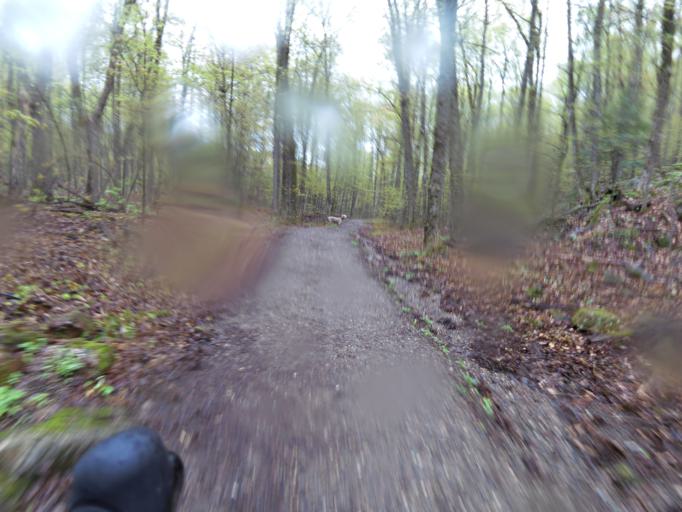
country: CA
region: Quebec
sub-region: Outaouais
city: Gatineau
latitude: 45.5054
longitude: -75.8190
